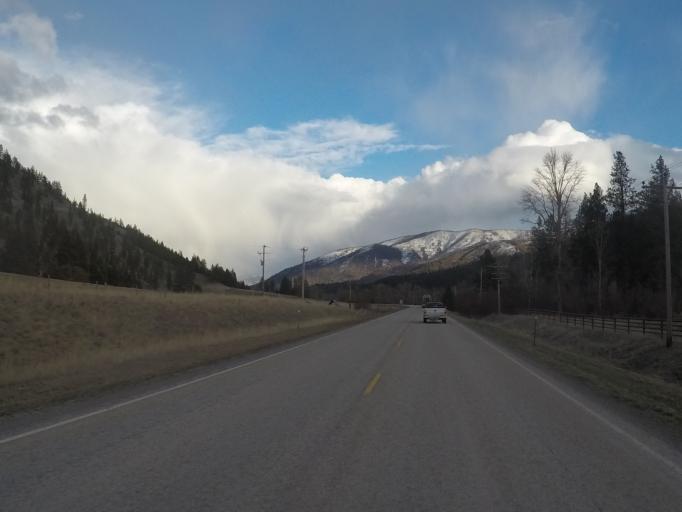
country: US
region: Montana
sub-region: Missoula County
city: Lolo
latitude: 46.7586
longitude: -114.2538
